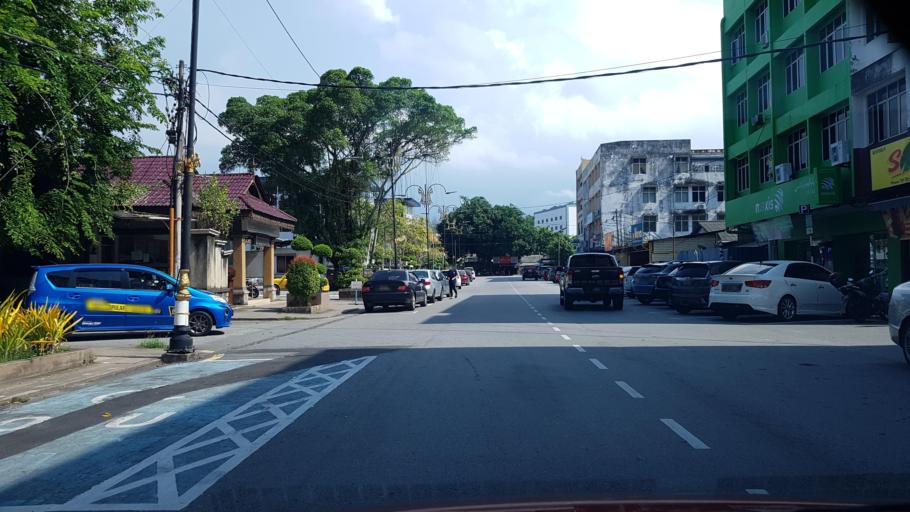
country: MY
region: Terengganu
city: Kuala Terengganu
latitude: 5.3295
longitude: 103.1372
